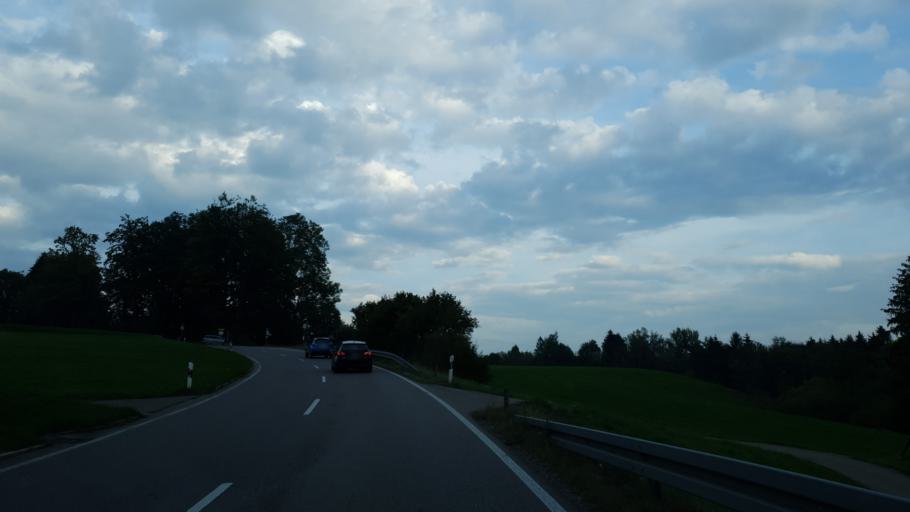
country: DE
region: Bavaria
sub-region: Swabia
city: Gestratz
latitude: 47.6650
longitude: 9.9450
